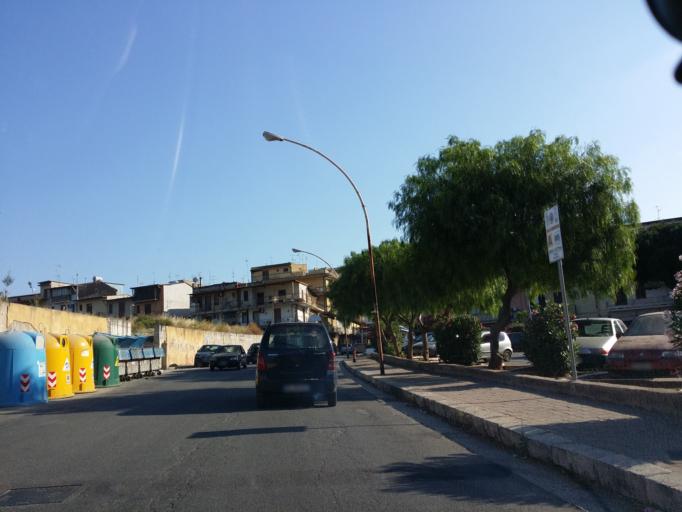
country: IT
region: Sicily
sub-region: Palermo
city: Misilmeri
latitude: 38.0297
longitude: 13.4497
